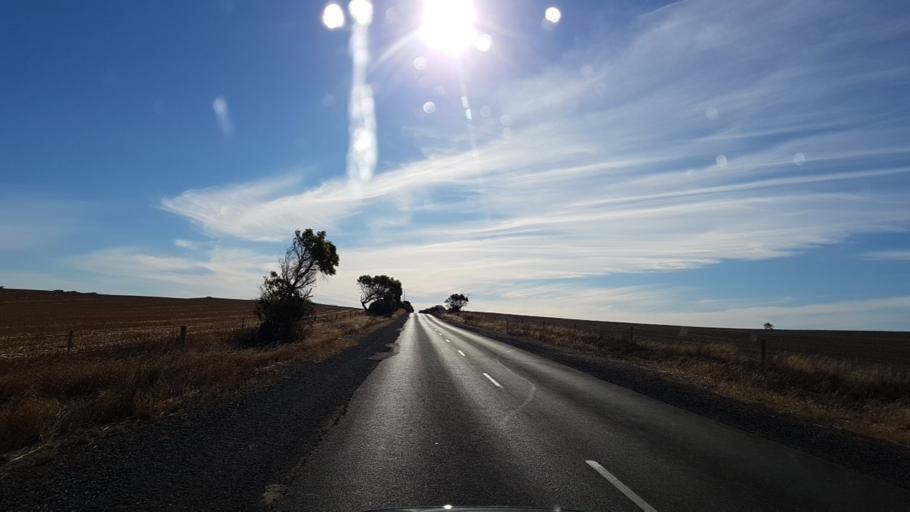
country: AU
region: South Australia
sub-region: Yorke Peninsula
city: Honiton
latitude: -34.9850
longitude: 137.2801
